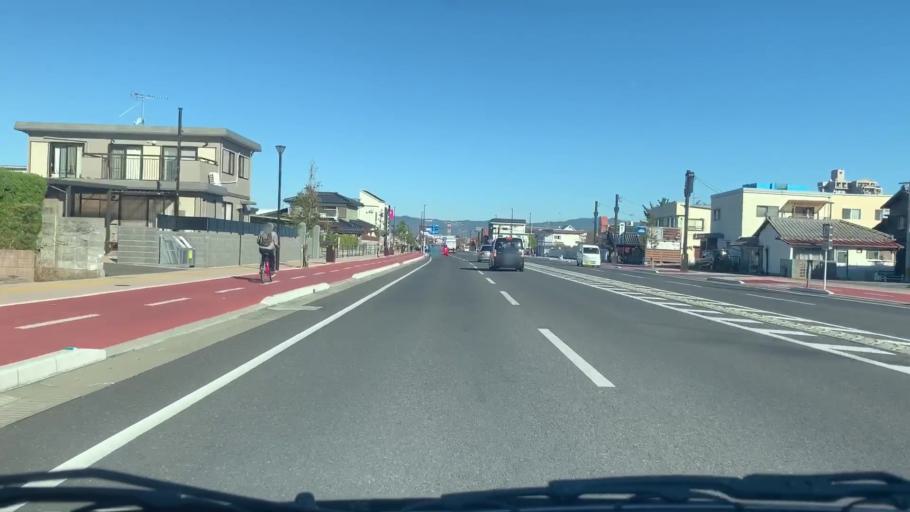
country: JP
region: Saga Prefecture
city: Saga-shi
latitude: 33.2470
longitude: 130.2929
